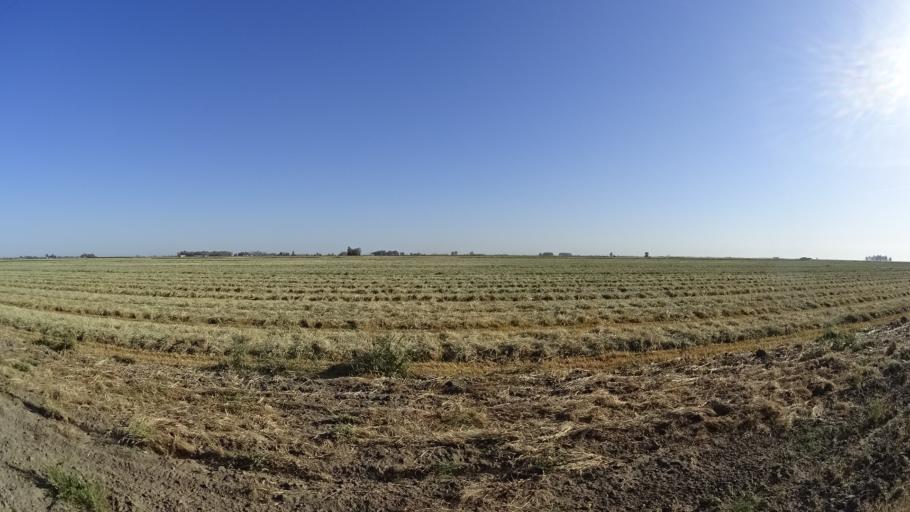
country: US
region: California
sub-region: Kings County
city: Stratford
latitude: 36.1748
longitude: -119.7884
